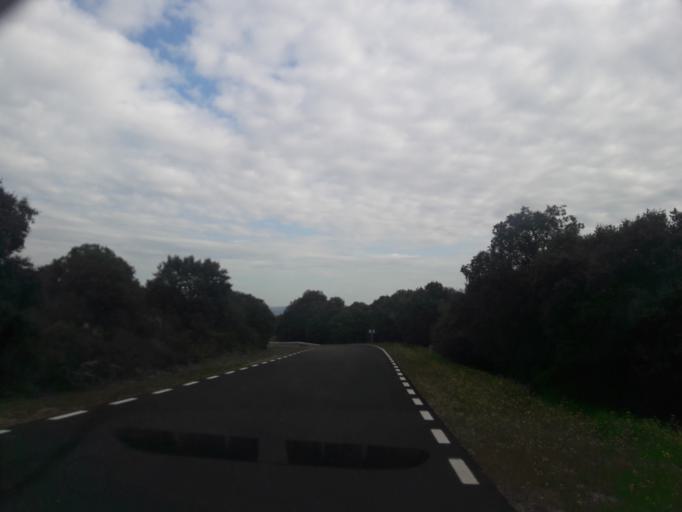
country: ES
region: Castille and Leon
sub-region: Provincia de Salamanca
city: Pastores
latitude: 40.5151
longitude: -6.5278
